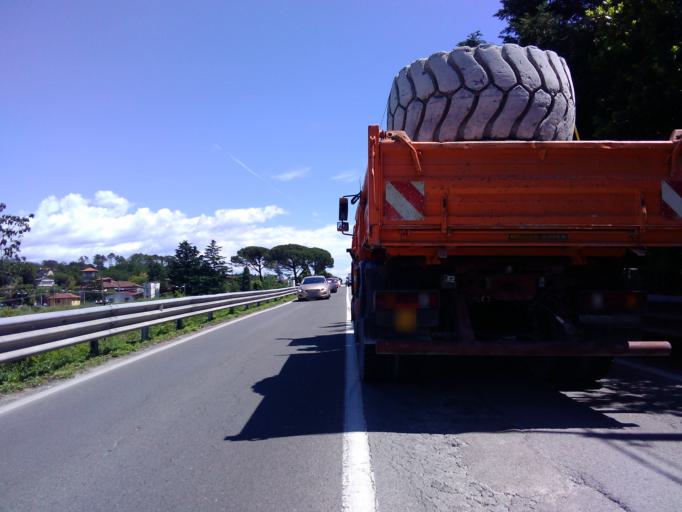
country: IT
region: Liguria
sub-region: Provincia di La Spezia
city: Santo Stefano di Magra
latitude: 44.1378
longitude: 9.9325
